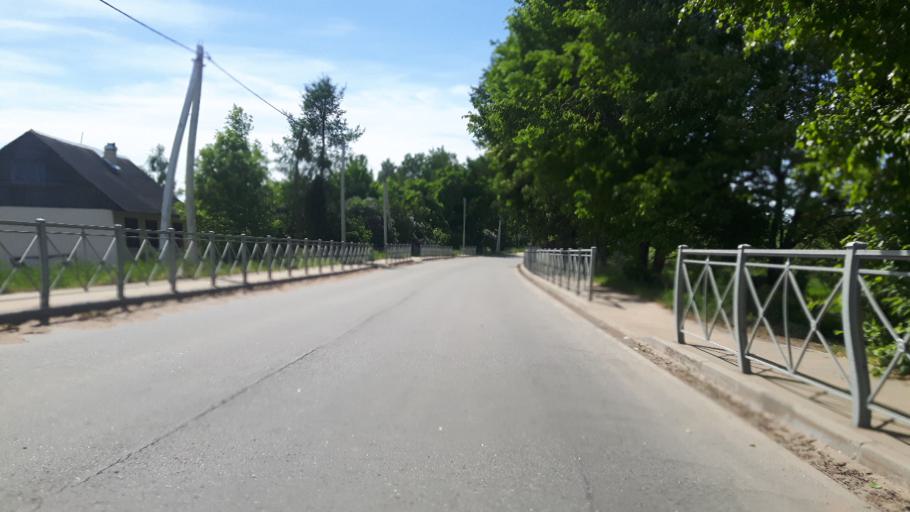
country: RU
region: Leningrad
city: Ust'-Luga
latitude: 59.5838
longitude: 28.1883
